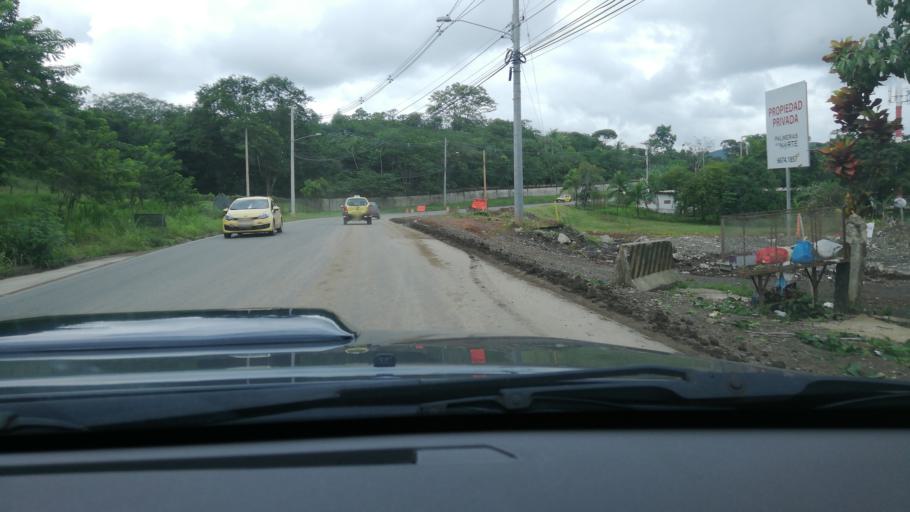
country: PA
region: Panama
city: San Miguelito
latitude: 9.0901
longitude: -79.4526
